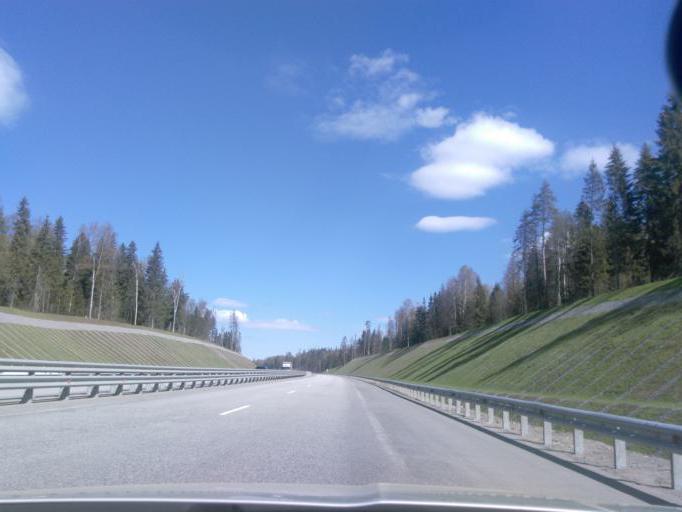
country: RU
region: Moskovskaya
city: Rzhavki
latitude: 56.0388
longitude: 37.2684
